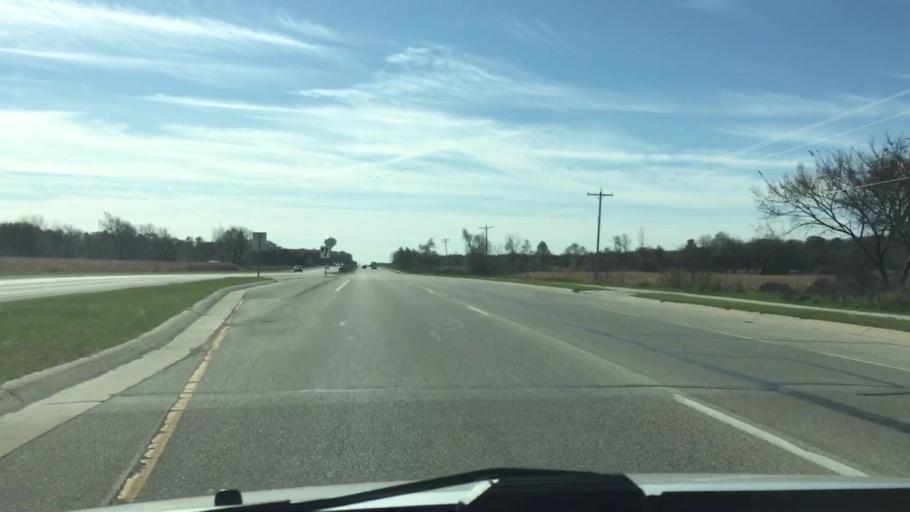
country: US
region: Wisconsin
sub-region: Waukesha County
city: Sussex
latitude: 43.1307
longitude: -88.2442
